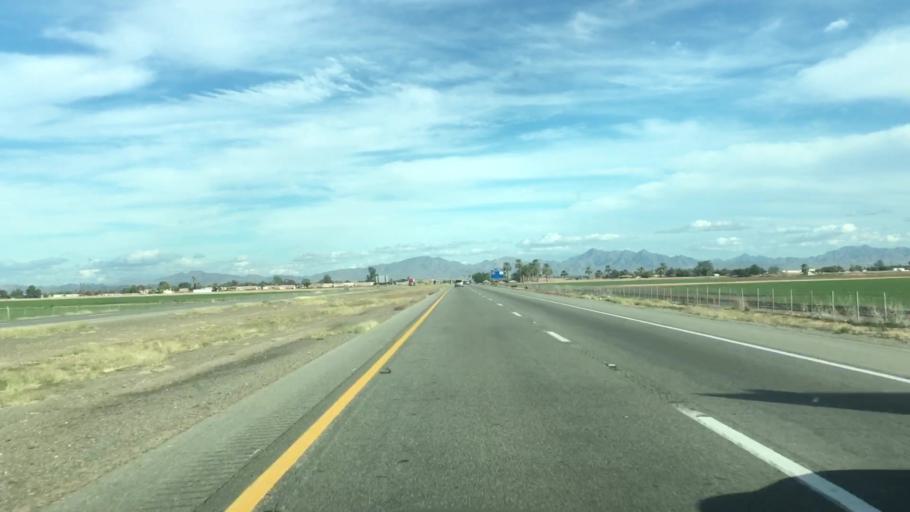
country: US
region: California
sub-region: Riverside County
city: Blythe
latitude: 33.6065
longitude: -114.6386
